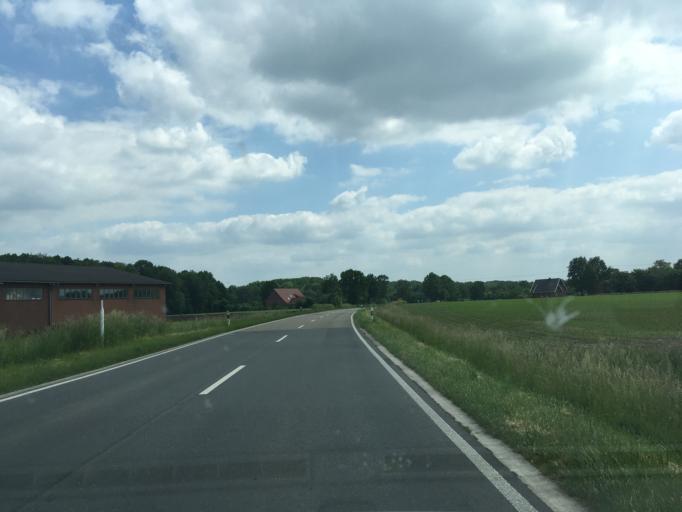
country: DE
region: North Rhine-Westphalia
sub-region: Regierungsbezirk Munster
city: Raesfeld
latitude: 51.7690
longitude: 6.8159
